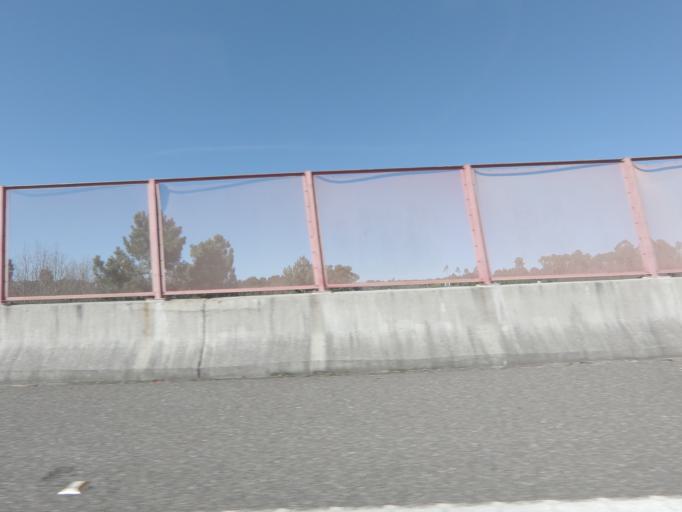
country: ES
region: Galicia
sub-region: Provincia de Ourense
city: Maside
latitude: 42.4216
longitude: -8.0160
